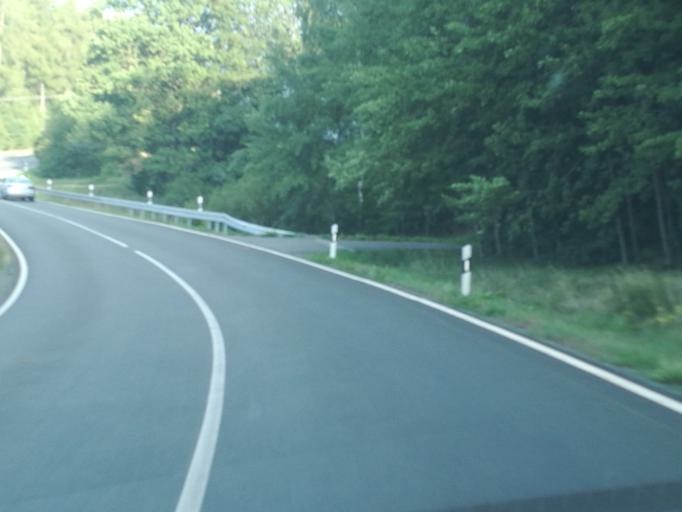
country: DE
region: Saxony
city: Adorf
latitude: 50.3356
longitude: 12.2159
